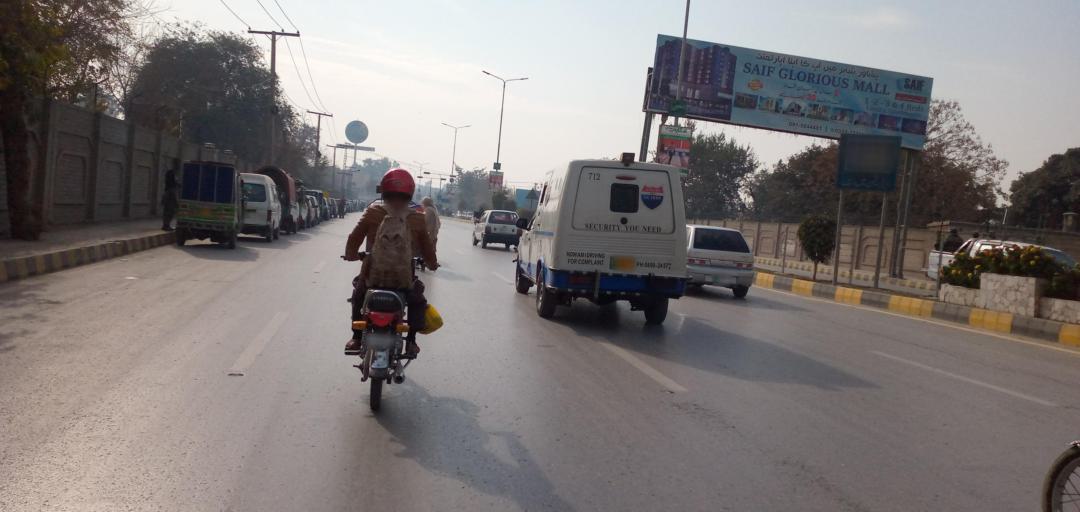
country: PK
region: Khyber Pakhtunkhwa
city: Peshawar
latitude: 34.0125
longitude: 71.5406
